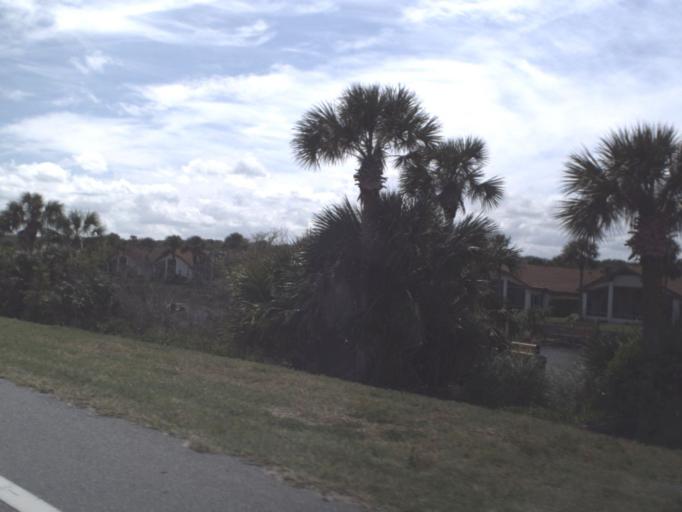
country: US
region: Florida
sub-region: Flagler County
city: Palm Coast
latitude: 29.6502
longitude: -81.2075
